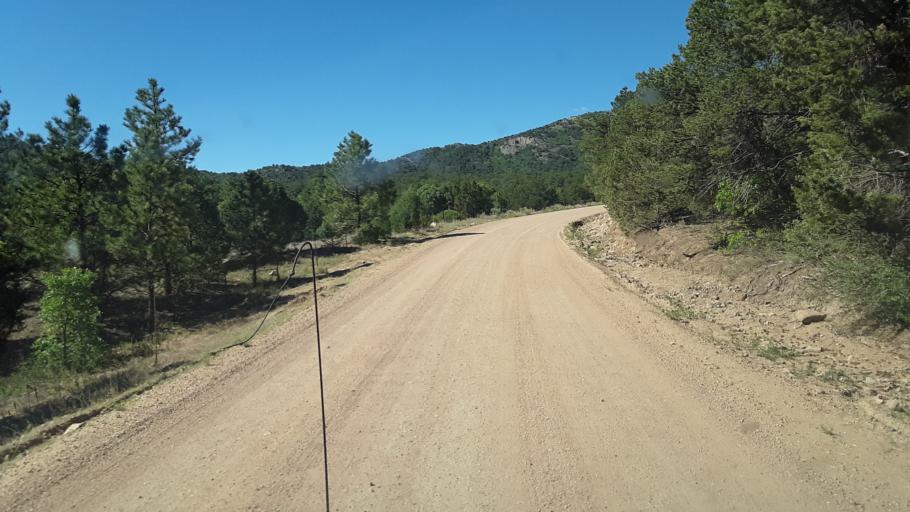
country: US
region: Colorado
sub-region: Custer County
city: Westcliffe
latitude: 38.2789
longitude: -105.5296
